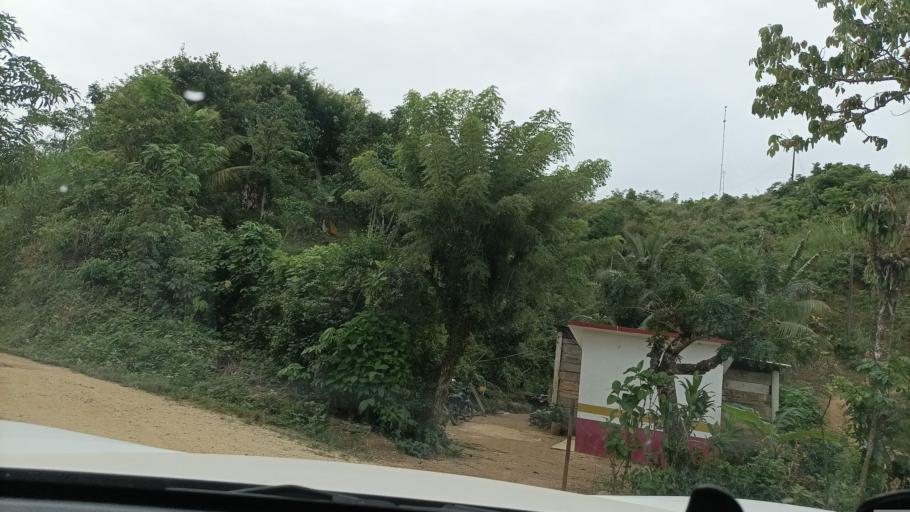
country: MX
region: Veracruz
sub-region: Uxpanapa
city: Poblado 10
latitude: 17.5647
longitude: -94.4251
